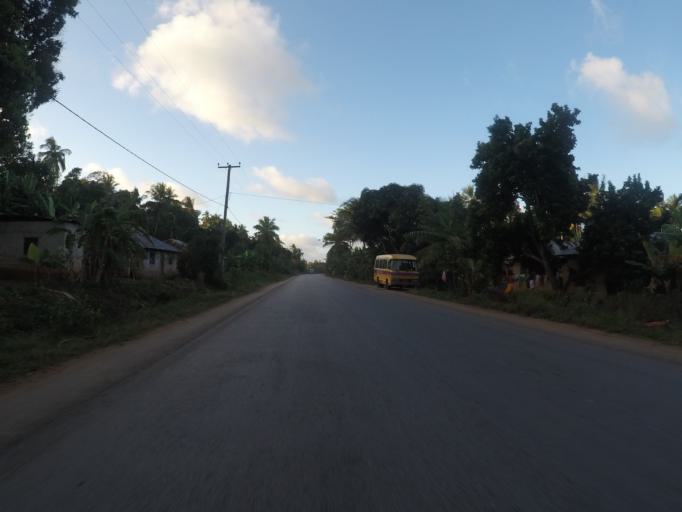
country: TZ
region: Zanzibar Central/South
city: Koani
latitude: -6.1331
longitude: 39.3252
